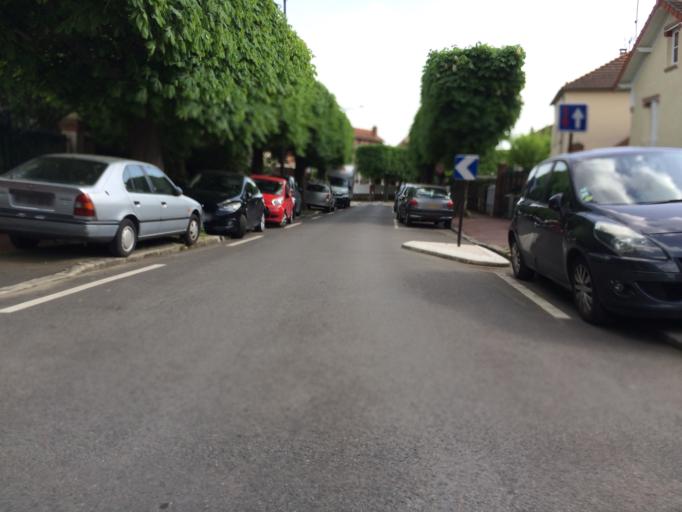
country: FR
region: Ile-de-France
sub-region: Departement du Val-de-Marne
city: Fresnes
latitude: 48.7619
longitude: 2.3107
